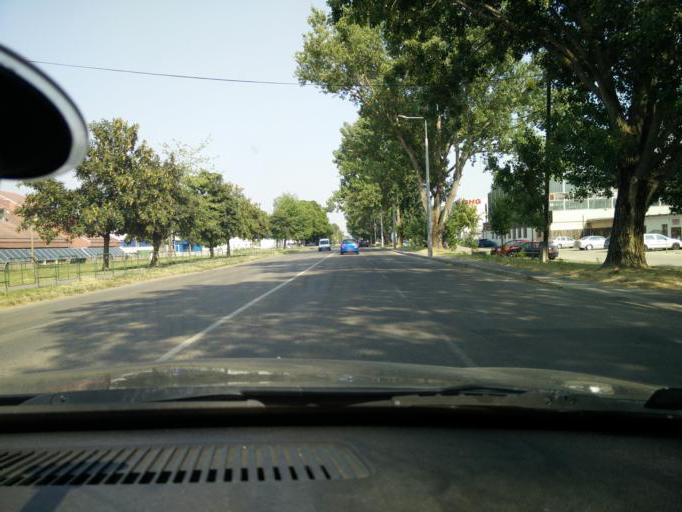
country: HU
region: Tolna
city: Szekszard
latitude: 46.3469
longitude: 18.7143
